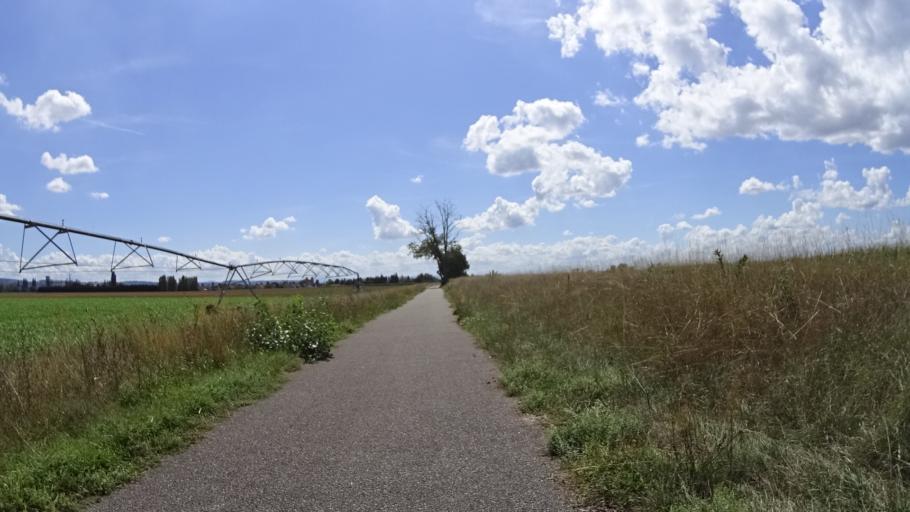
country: FR
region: Alsace
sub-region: Departement du Haut-Rhin
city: Ottmarsheim
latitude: 47.7990
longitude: 7.5051
